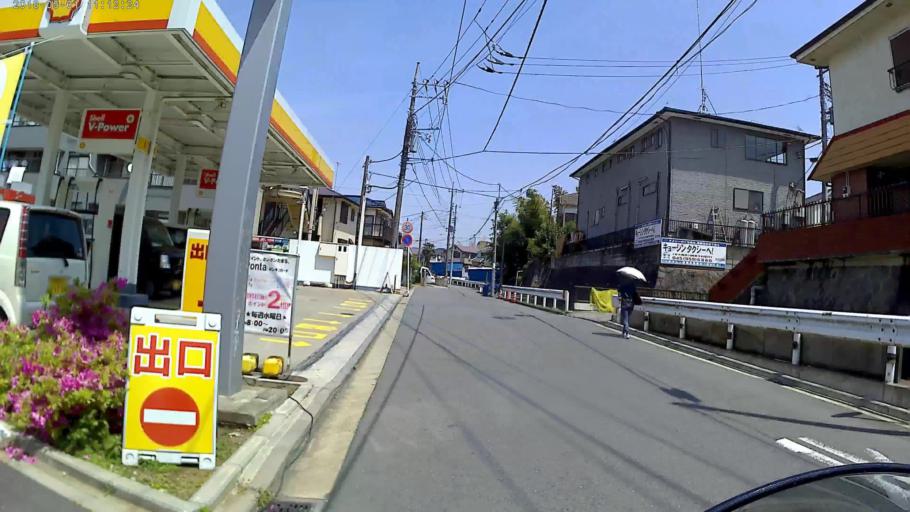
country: JP
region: Kanagawa
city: Minami-rinkan
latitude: 35.4887
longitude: 139.5420
